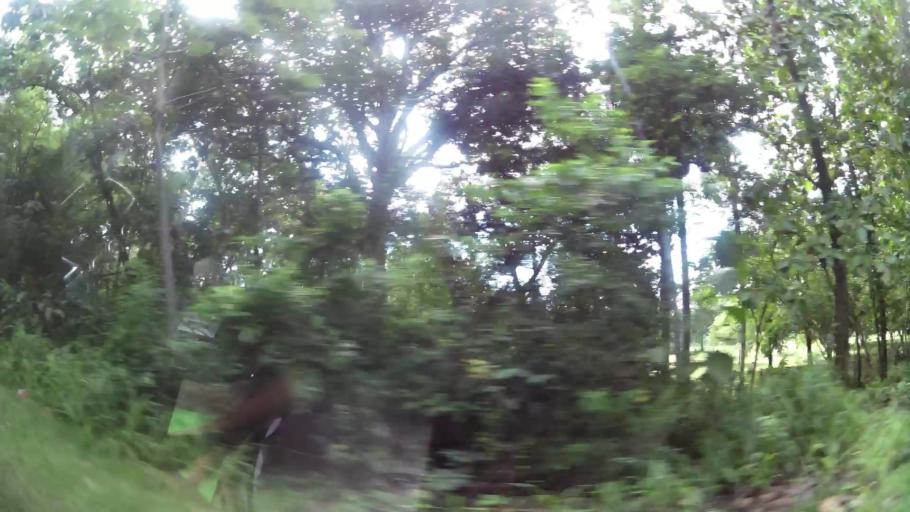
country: PA
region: Panama
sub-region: Distrito de Panama
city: Paraiso
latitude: 9.0139
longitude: -79.5994
